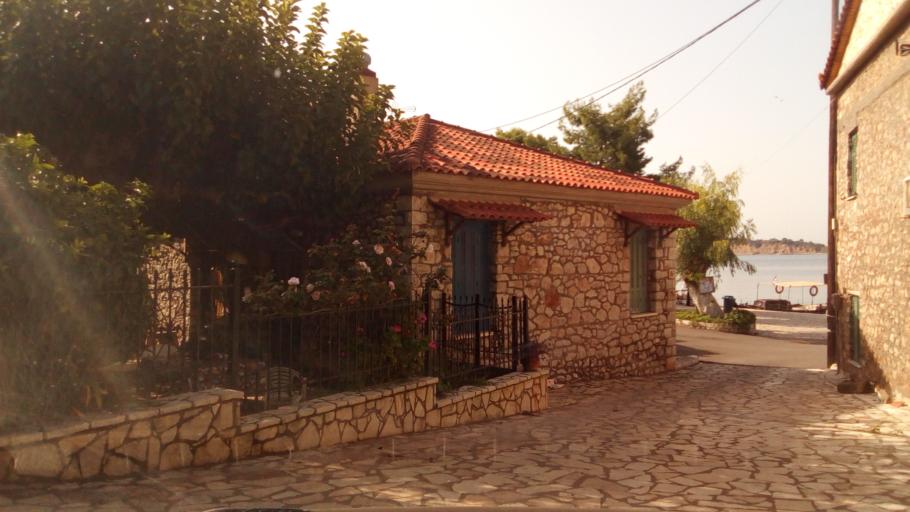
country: GR
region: West Greece
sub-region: Nomos Aitolias kai Akarnanias
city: Nafpaktos
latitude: 38.4066
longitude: 21.9419
